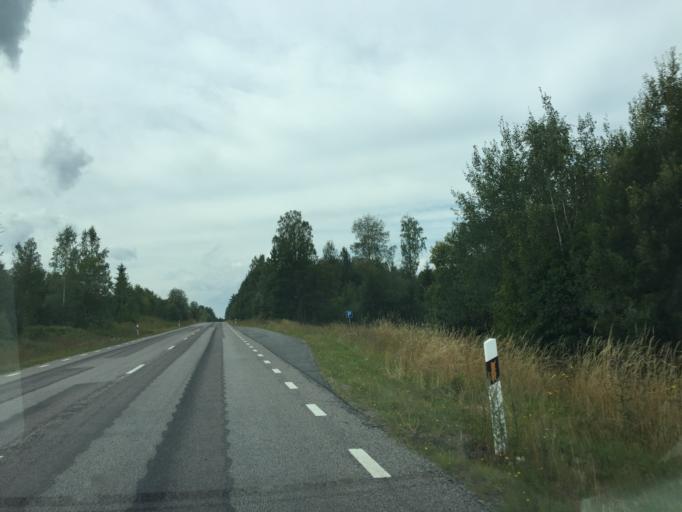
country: SE
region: Uppsala
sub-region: Tierps Kommun
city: Tierp
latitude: 60.3605
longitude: 17.3908
